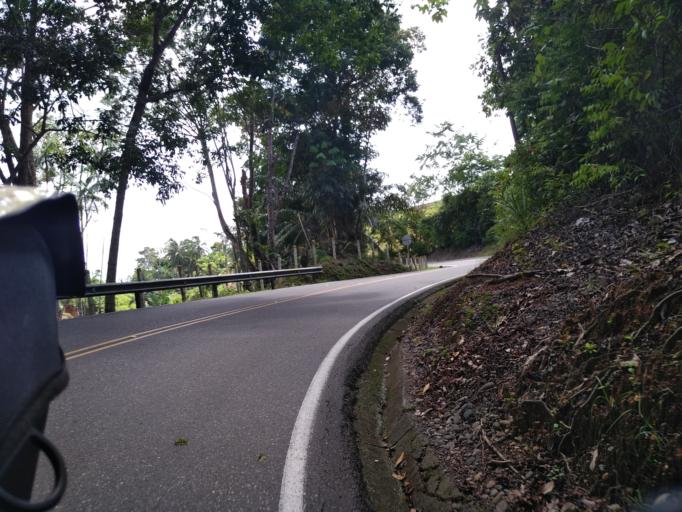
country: CO
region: Santander
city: Cimitarra
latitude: 6.4381
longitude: -74.0157
